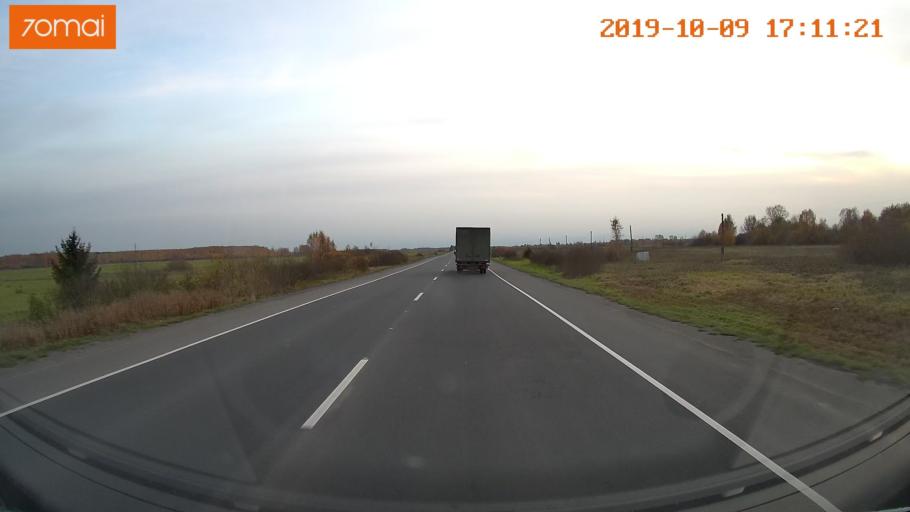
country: RU
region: Ivanovo
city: Privolzhsk
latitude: 57.3441
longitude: 41.2508
